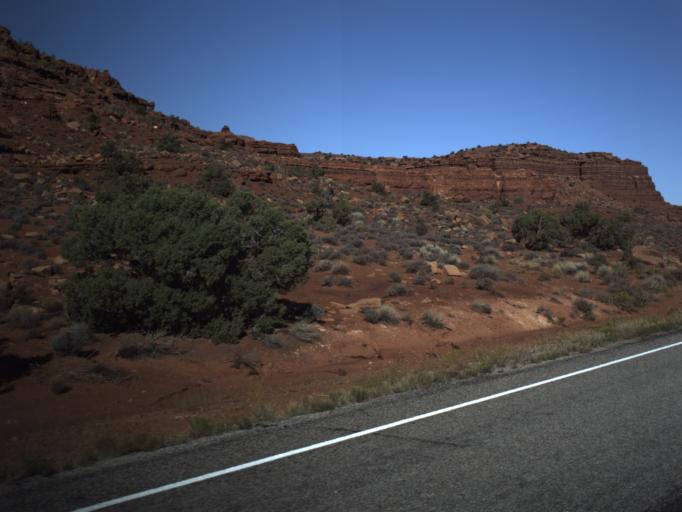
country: US
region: Utah
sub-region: San Juan County
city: Blanding
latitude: 37.7764
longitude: -110.2895
